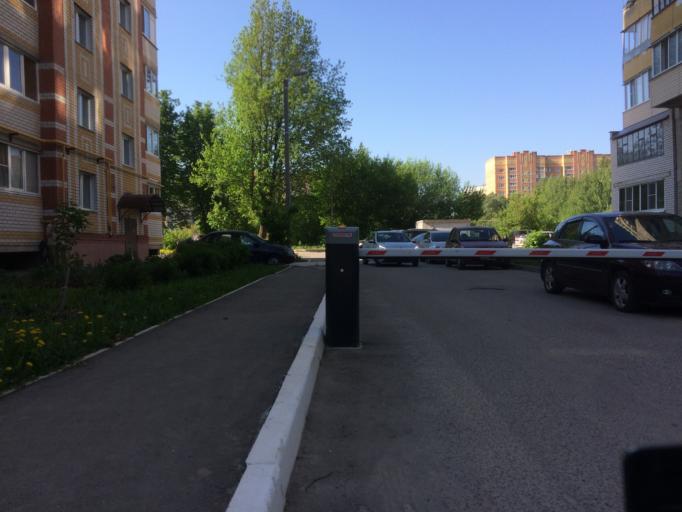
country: RU
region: Mariy-El
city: Yoshkar-Ola
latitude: 56.6459
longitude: 47.8513
